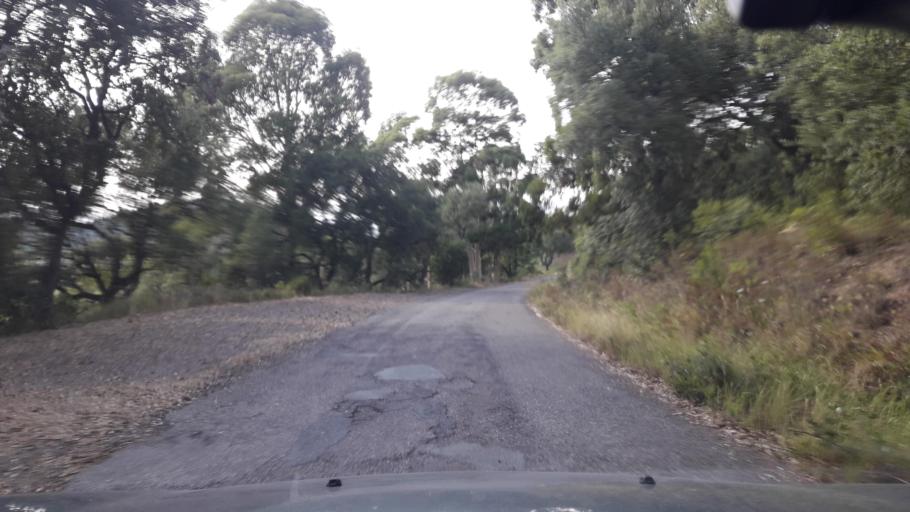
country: FR
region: Provence-Alpes-Cote d'Azur
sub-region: Departement du Var
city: Saint-Raphael
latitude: 43.4990
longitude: 6.7989
